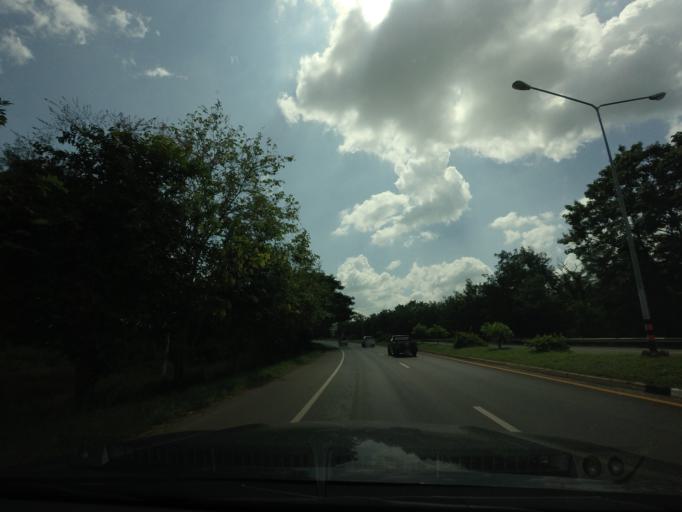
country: TH
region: Phetchabun
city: Nong Phai
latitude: 16.1185
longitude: 101.0369
